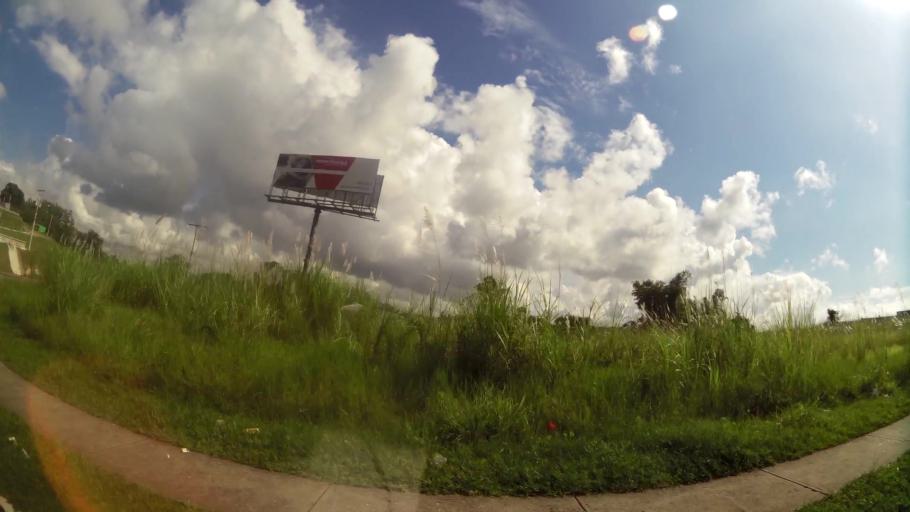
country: PA
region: Panama
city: Nuevo Arraijan
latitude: 8.9058
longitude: -79.7476
